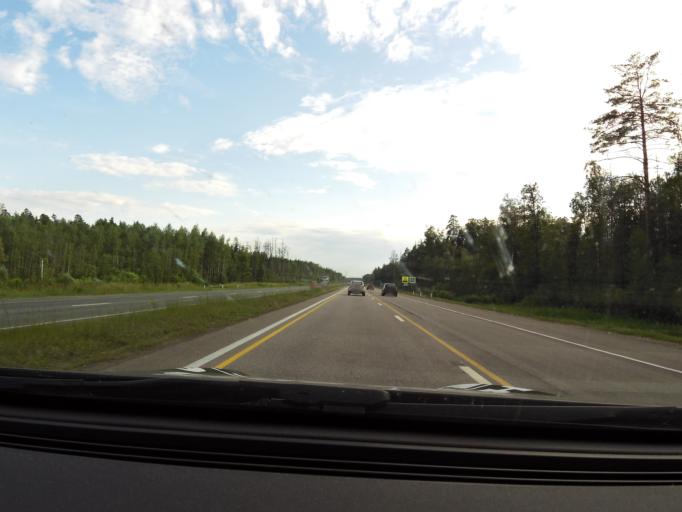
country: RU
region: Vladimir
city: Kameshkovo
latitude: 56.1651
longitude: 40.9334
